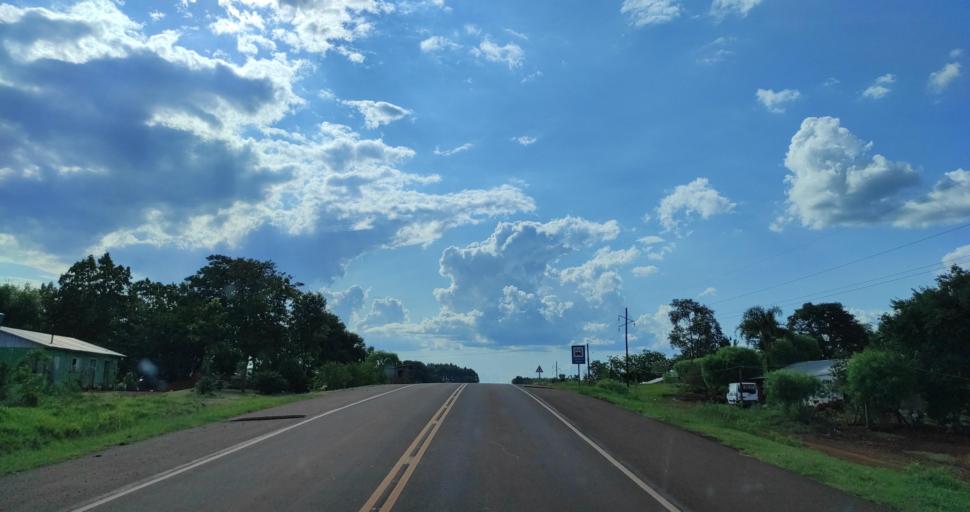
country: AR
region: Misiones
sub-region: Departamento de San Pedro
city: San Pedro
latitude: -26.3722
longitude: -53.9352
